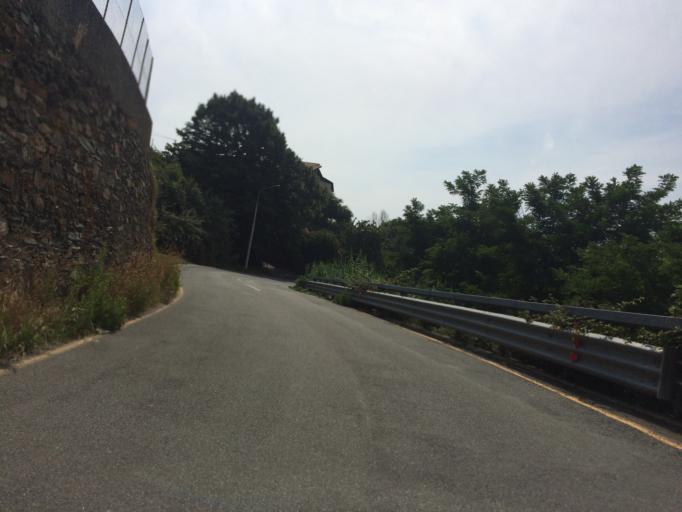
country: IT
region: Liguria
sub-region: Provincia di Savona
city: San Giovanni
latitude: 44.3913
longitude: 8.5121
